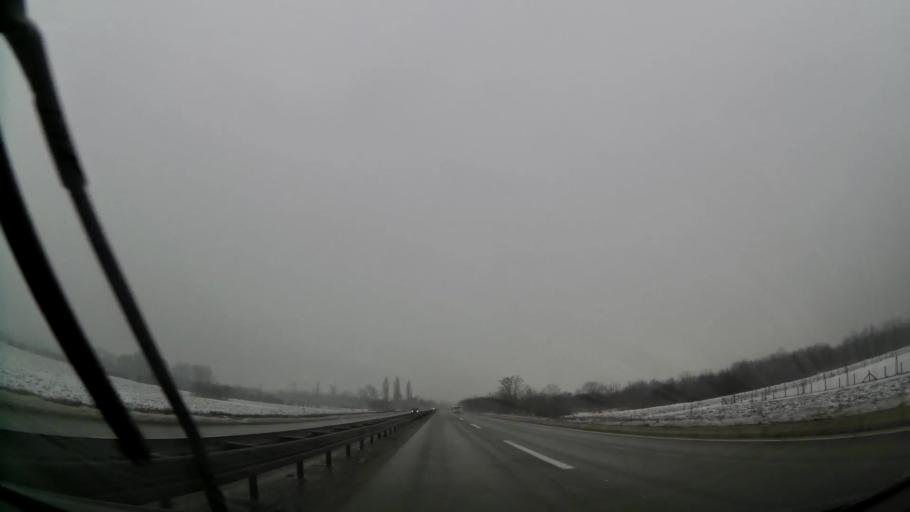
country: RS
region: Central Serbia
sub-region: Belgrade
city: Cukarica
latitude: 44.7635
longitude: 20.3896
